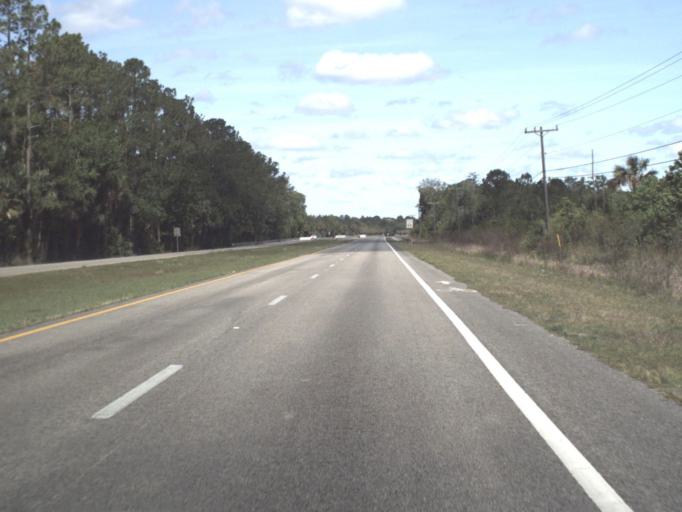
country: US
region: Florida
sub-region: Flagler County
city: Bunnell
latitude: 29.4490
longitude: -81.2431
